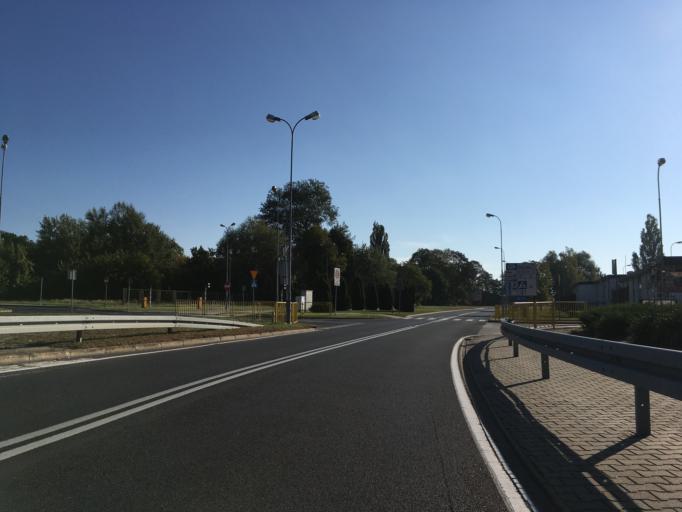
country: PL
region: Lubusz
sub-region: Powiat gorzowski
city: Kostrzyn nad Odra
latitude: 52.5812
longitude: 14.6352
